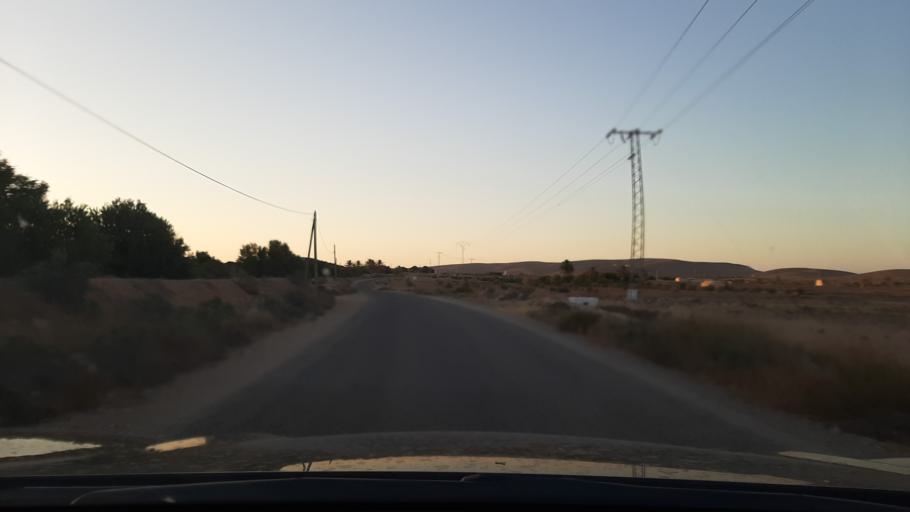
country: TN
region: Qabis
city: Matmata
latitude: 33.5562
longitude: 10.1852
